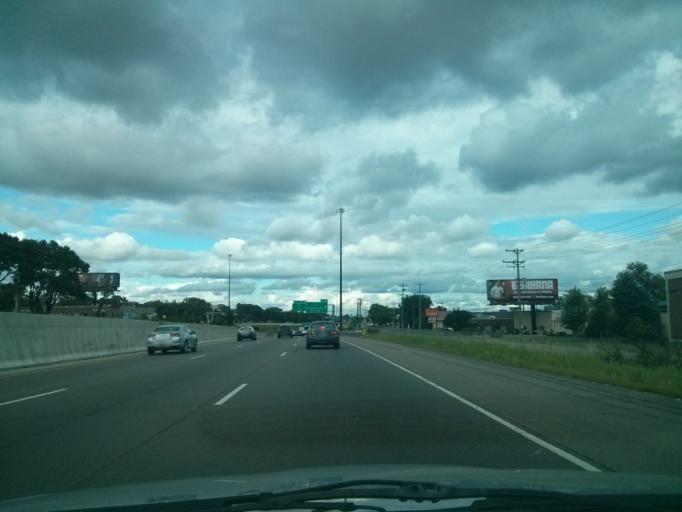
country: US
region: Minnesota
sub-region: Hennepin County
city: Richfield
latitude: 44.8617
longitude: -93.2723
